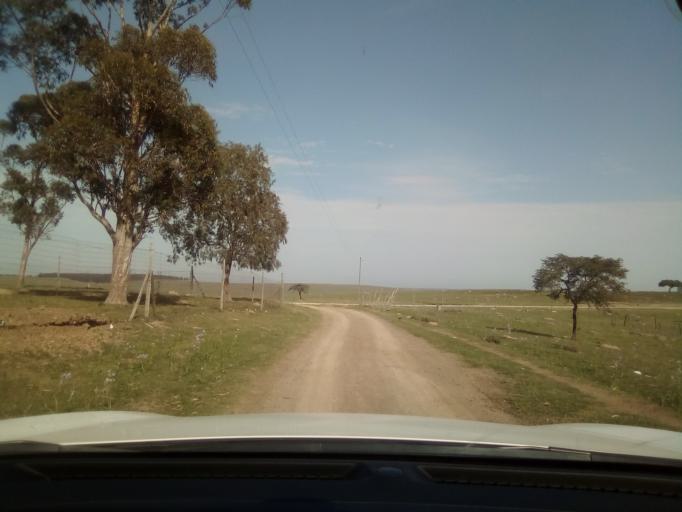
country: ZA
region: Eastern Cape
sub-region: Buffalo City Metropolitan Municipality
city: Bhisho
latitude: -32.9863
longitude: 27.2571
